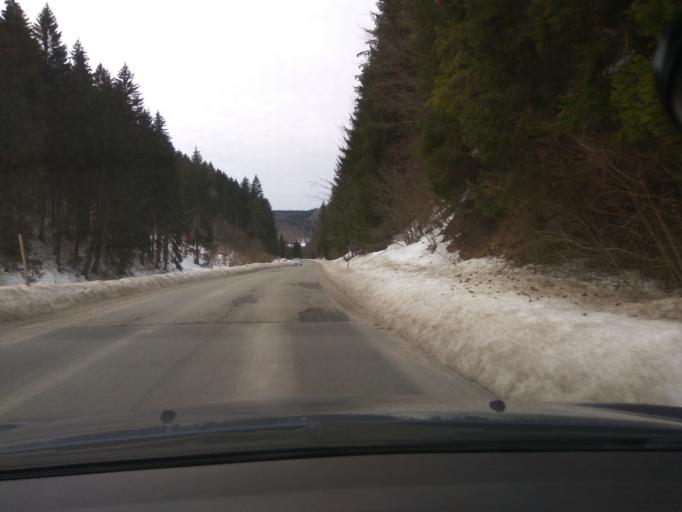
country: SK
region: Nitriansky
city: Bojnice
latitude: 48.9475
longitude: 18.5021
